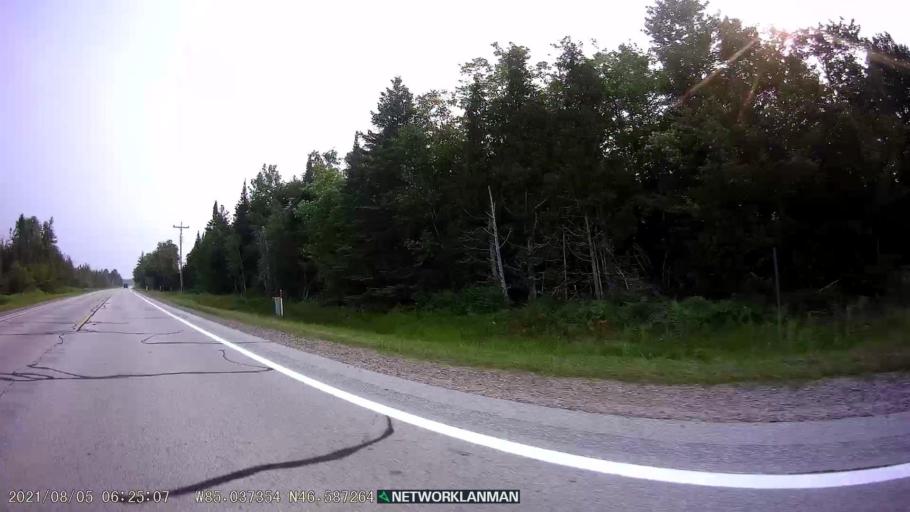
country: US
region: Michigan
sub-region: Luce County
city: Newberry
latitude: 46.5878
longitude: -85.0369
